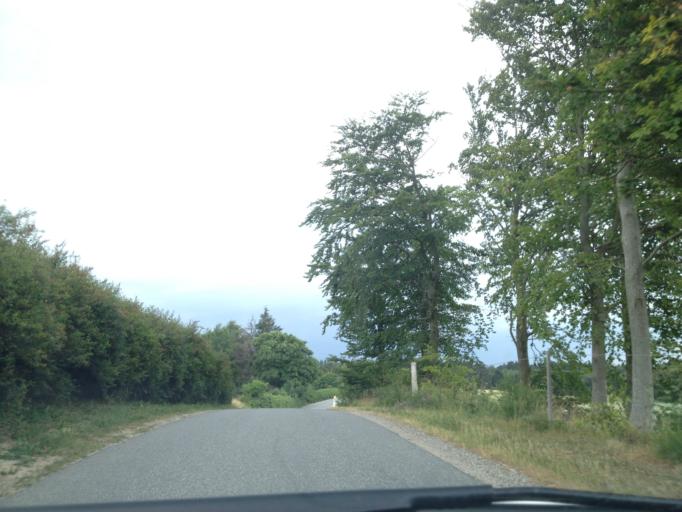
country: DK
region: Central Jutland
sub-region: Syddjurs Kommune
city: Ebeltoft
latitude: 56.1579
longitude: 10.6941
